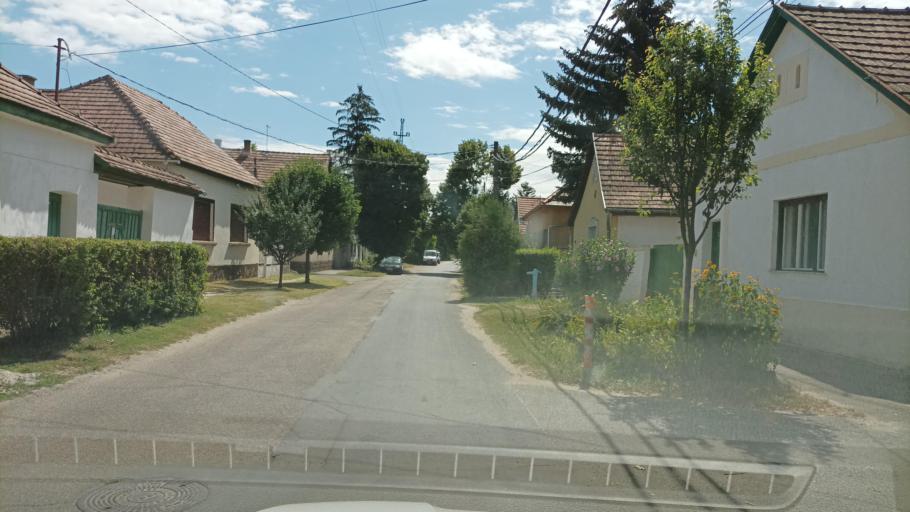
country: HU
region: Pest
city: Kismaros
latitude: 47.8082
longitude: 19.0052
